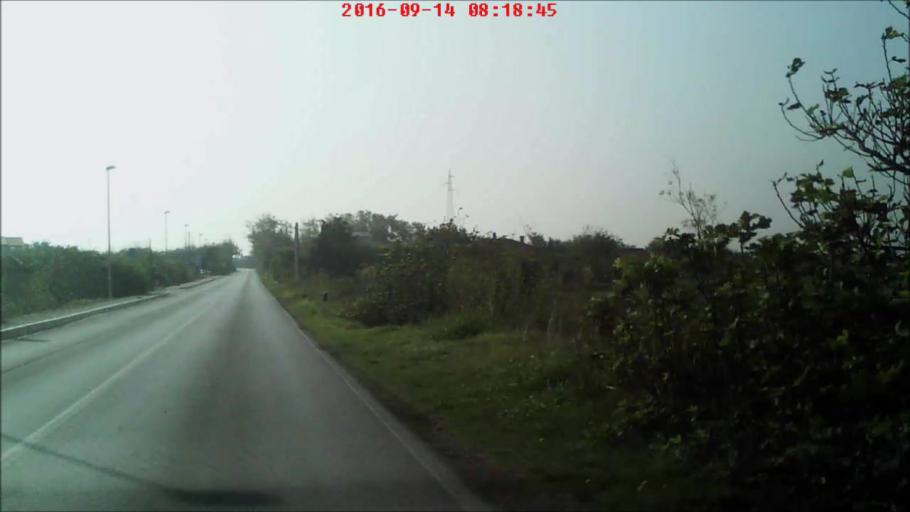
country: HR
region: Zadarska
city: Nin
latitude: 44.2372
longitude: 15.1853
